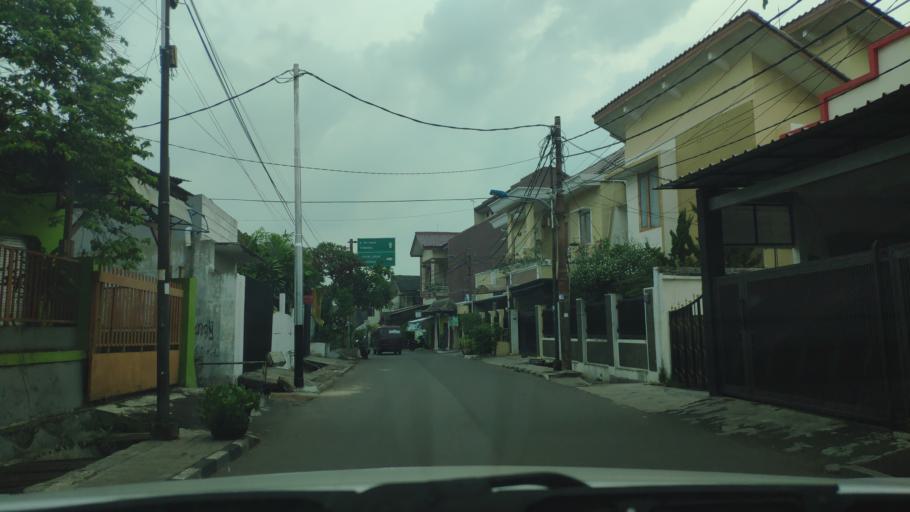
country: ID
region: Jakarta Raya
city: Jakarta
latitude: -6.1935
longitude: 106.7937
